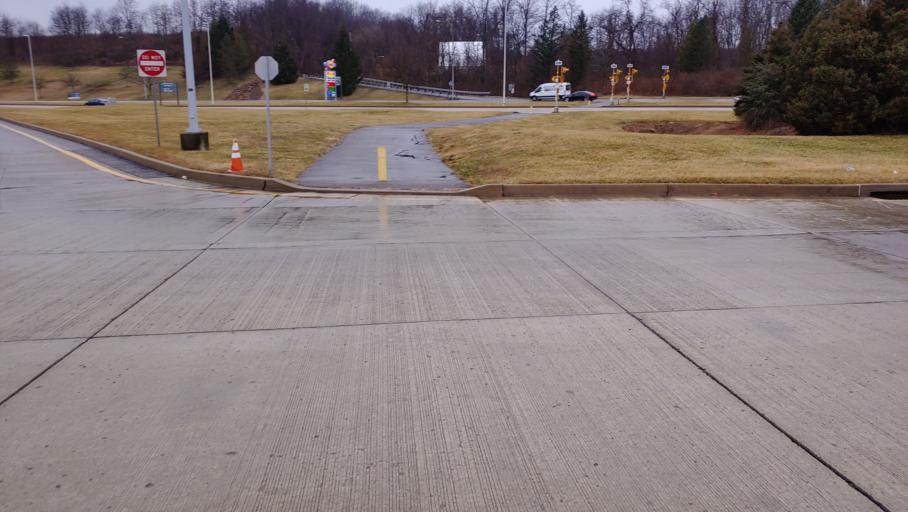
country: US
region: Pennsylvania
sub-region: Allegheny County
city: Carnot-Moon
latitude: 40.4980
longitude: -80.2651
